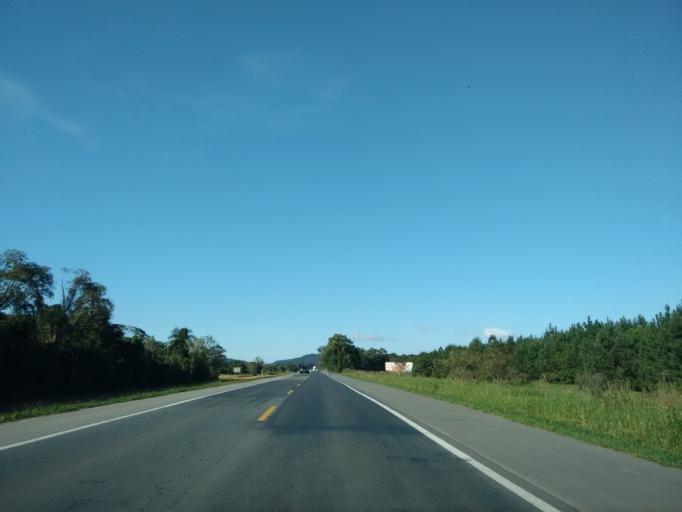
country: BR
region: Santa Catarina
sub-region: Joinville
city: Joinville
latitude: -26.4500
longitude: -48.8572
